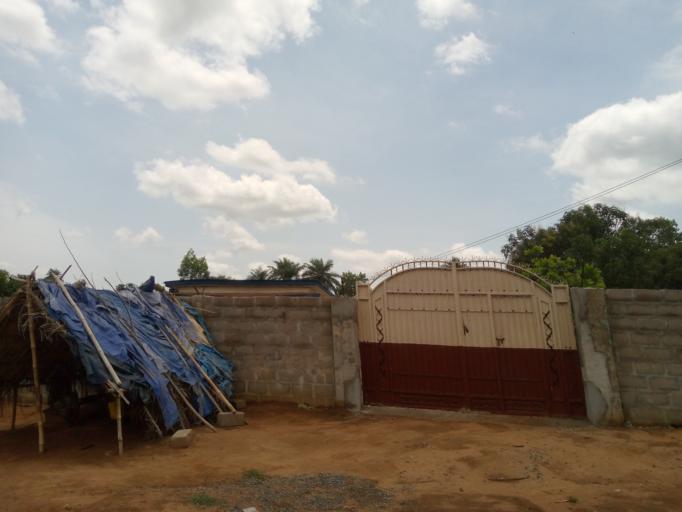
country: SL
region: Western Area
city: Waterloo
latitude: 8.3374
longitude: -12.9937
